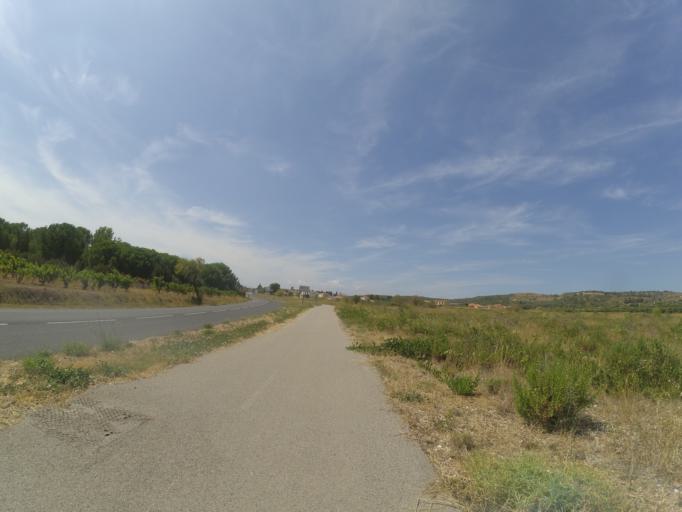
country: FR
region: Languedoc-Roussillon
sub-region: Departement des Pyrenees-Orientales
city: Baixas
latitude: 42.7543
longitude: 2.8208
